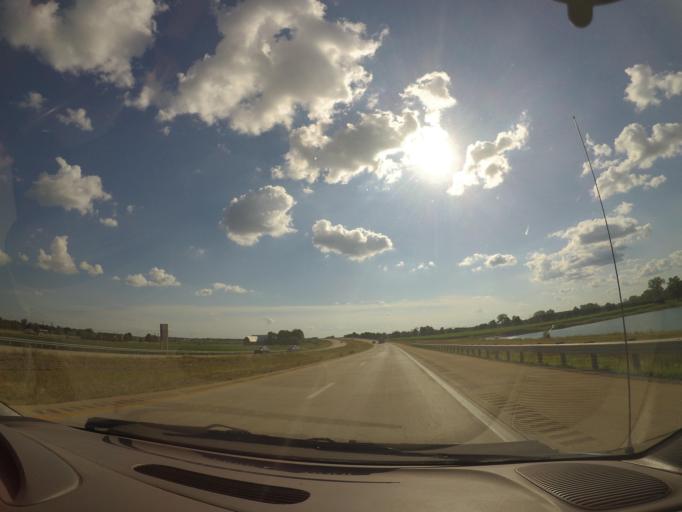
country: US
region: Ohio
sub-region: Lucas County
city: Waterville
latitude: 41.5243
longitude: -83.7351
